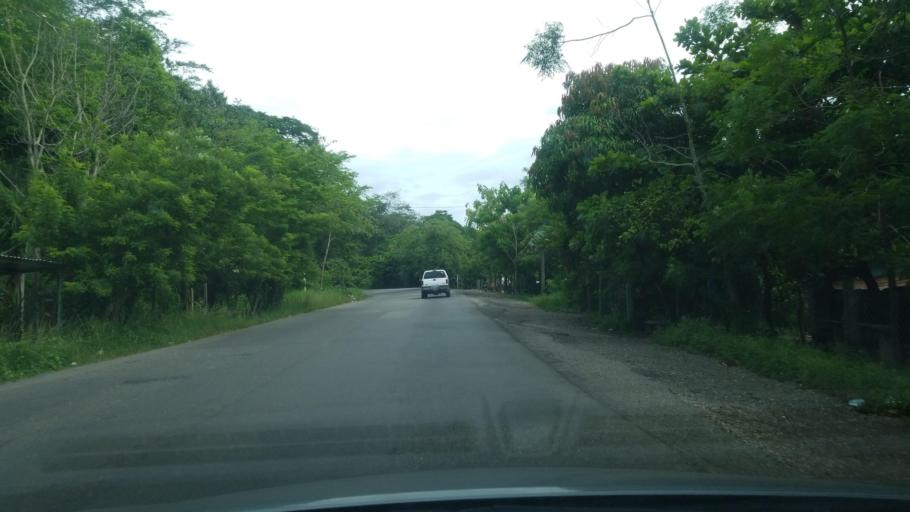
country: HN
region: Santa Barbara
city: Camalote
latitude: 15.3306
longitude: -88.2957
